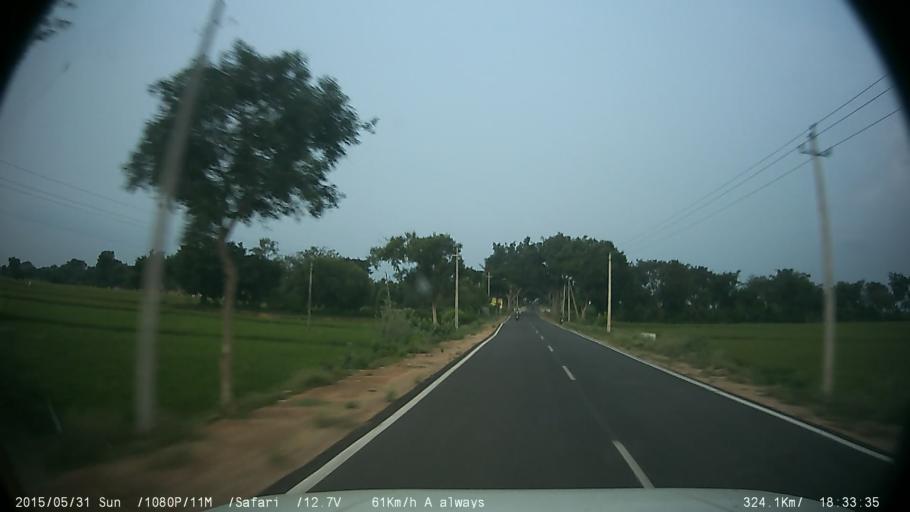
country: IN
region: Karnataka
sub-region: Mysore
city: Nanjangud
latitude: 12.1401
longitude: 76.7519
